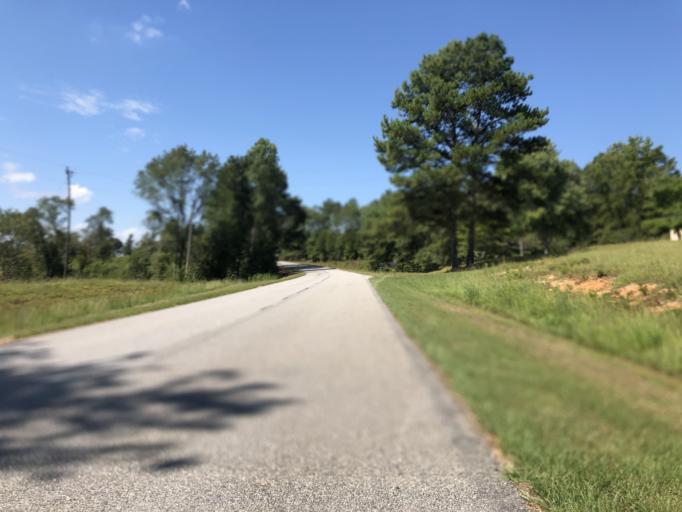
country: US
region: Georgia
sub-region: Heard County
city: Franklin
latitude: 33.3755
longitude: -85.0149
